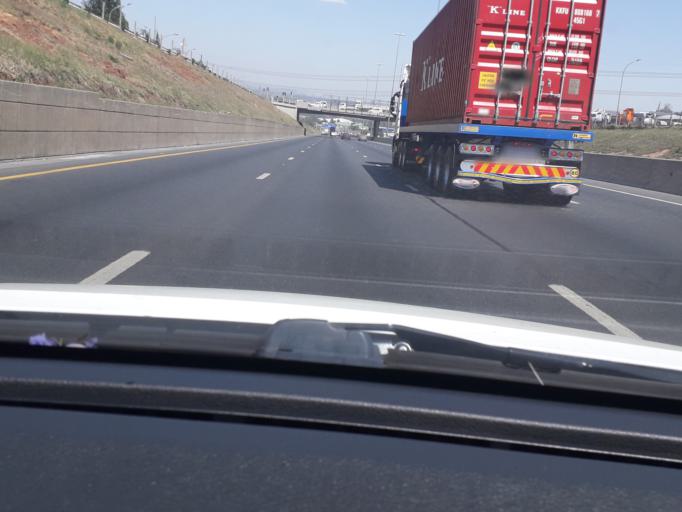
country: ZA
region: Gauteng
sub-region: Ekurhuleni Metropolitan Municipality
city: Germiston
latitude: -26.1653
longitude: 28.1824
